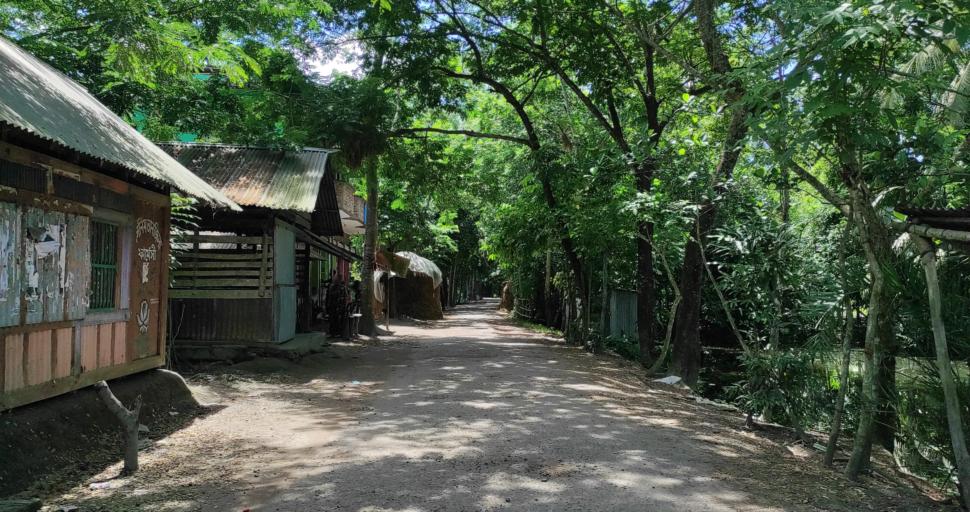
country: BD
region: Barisal
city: Gaurnadi
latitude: 22.9182
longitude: 90.0811
